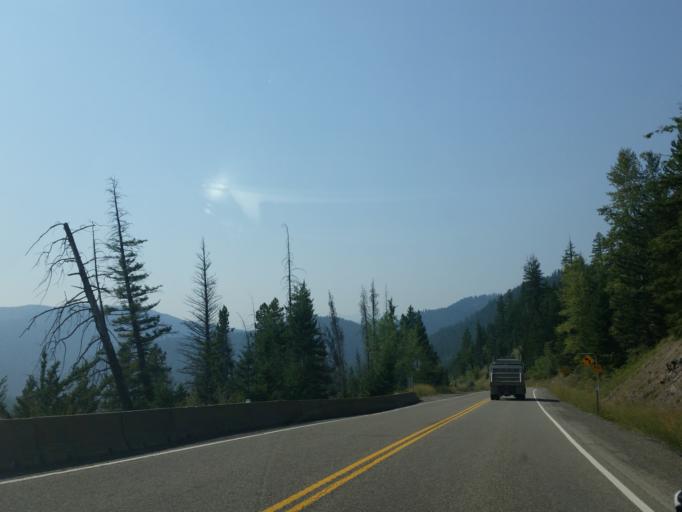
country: CA
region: British Columbia
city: Princeton
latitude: 49.2070
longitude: -120.5552
